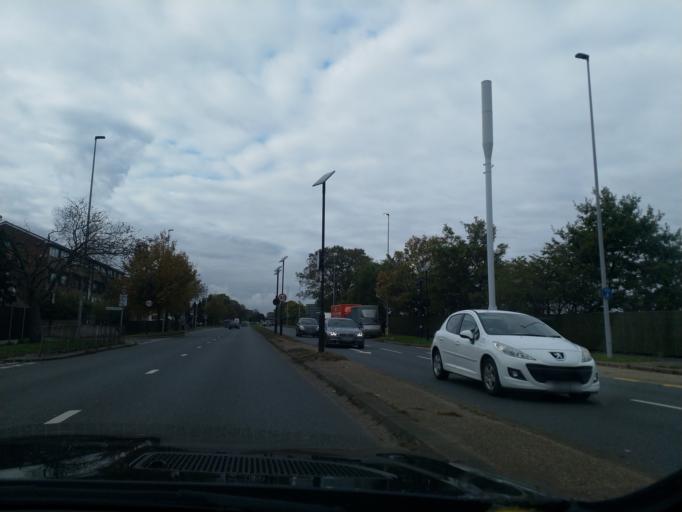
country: GB
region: England
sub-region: Greater London
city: Feltham
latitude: 51.4758
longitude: -0.3969
